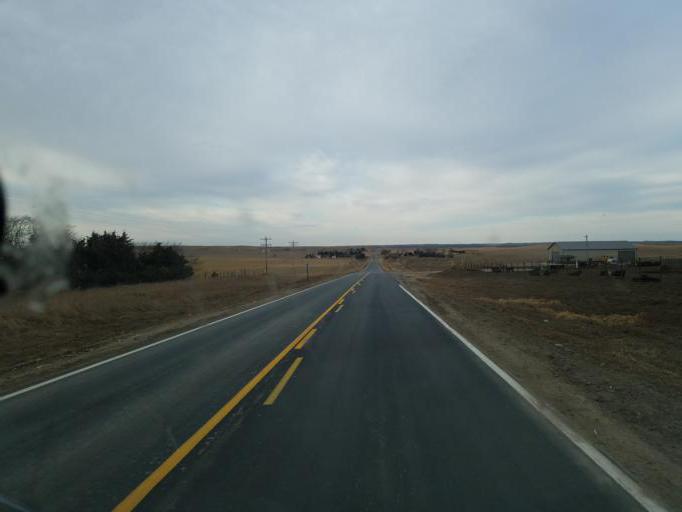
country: US
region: Nebraska
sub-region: Knox County
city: Center
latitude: 42.5971
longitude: -97.7968
